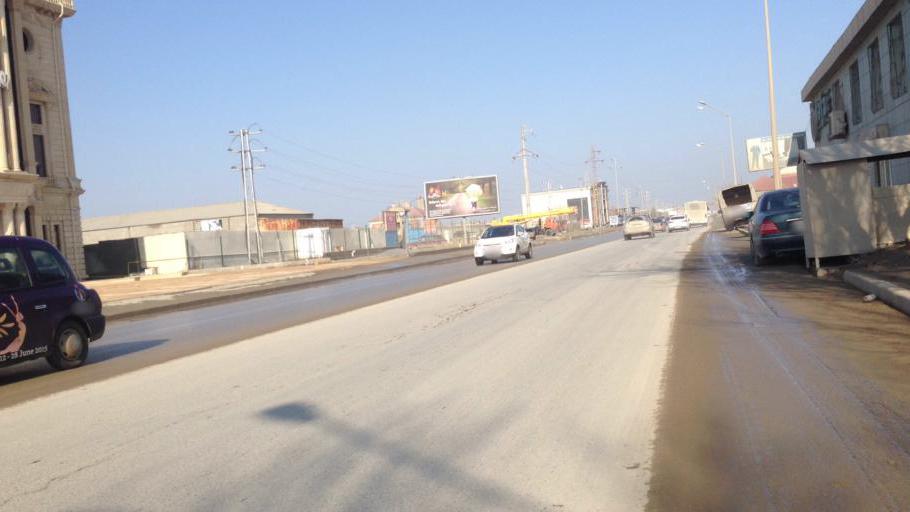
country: AZ
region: Baki
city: Binagadi
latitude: 40.4457
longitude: 49.8442
